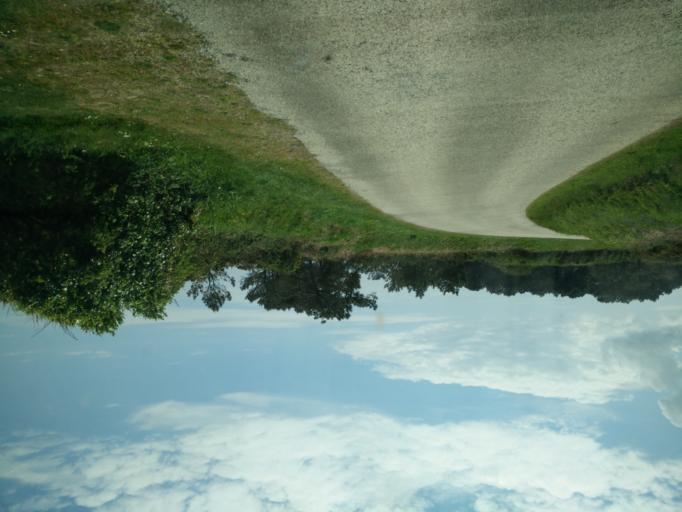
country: FR
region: Brittany
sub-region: Departement du Finistere
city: Roscanvel
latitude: 48.3224
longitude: -4.5756
